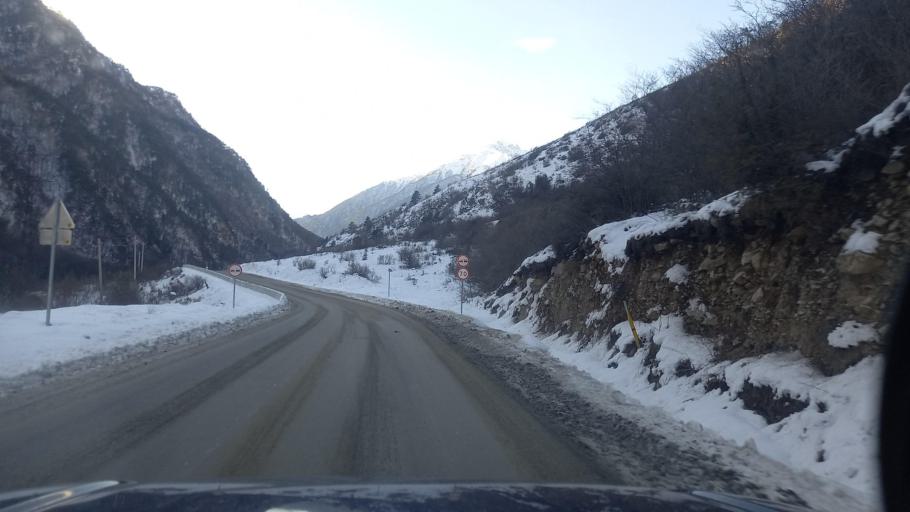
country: RU
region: North Ossetia
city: Chikola
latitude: 42.9783
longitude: 43.7658
